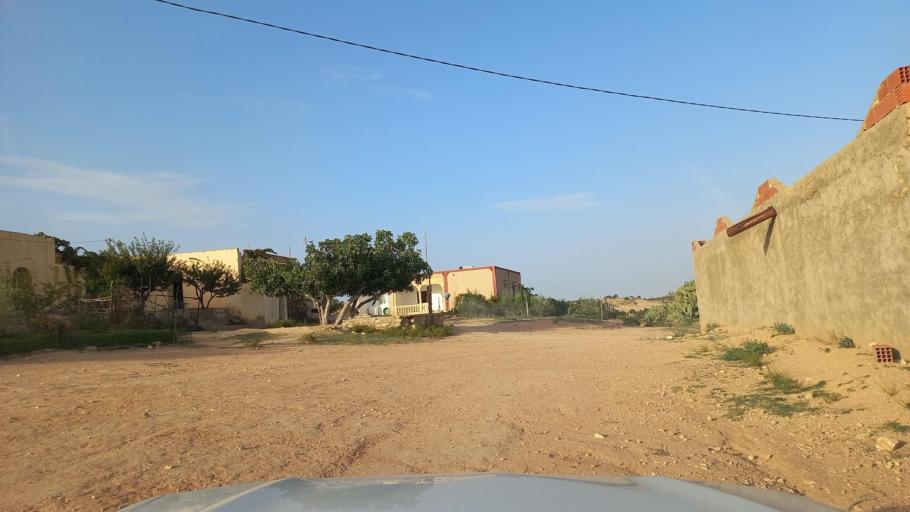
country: TN
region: Al Qasrayn
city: Sbiba
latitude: 35.4069
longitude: 8.8964
